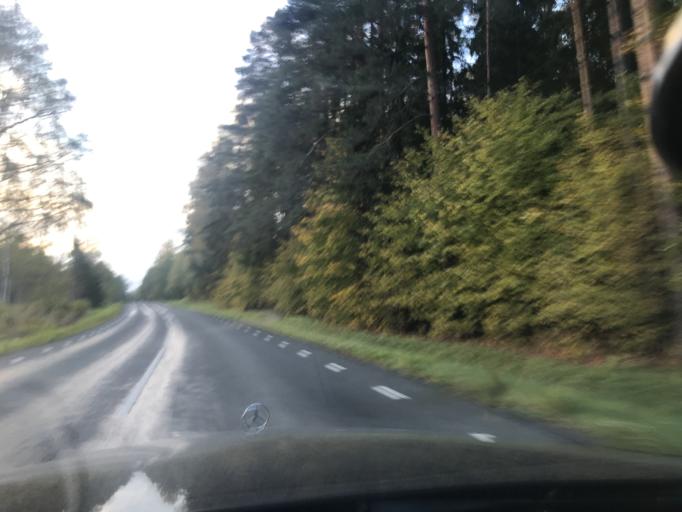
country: EE
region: Vorumaa
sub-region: Antsla vald
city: Vana-Antsla
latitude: 57.8807
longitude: 26.5757
